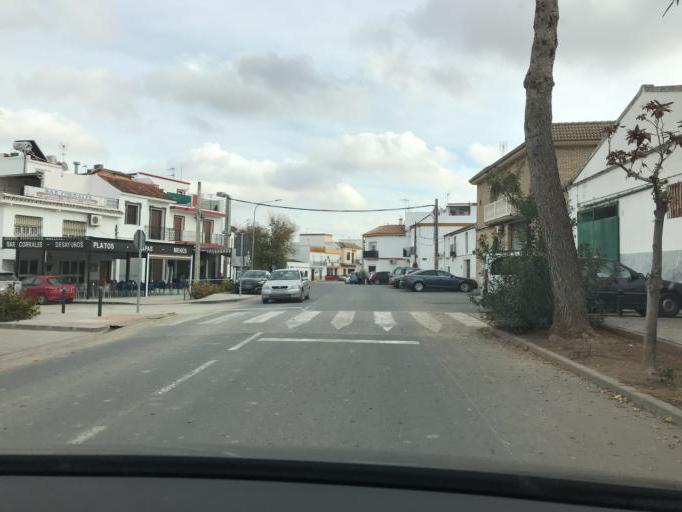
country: ES
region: Andalusia
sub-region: Provincia de Sevilla
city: La Lantejuela
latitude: 37.3554
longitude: -5.2260
